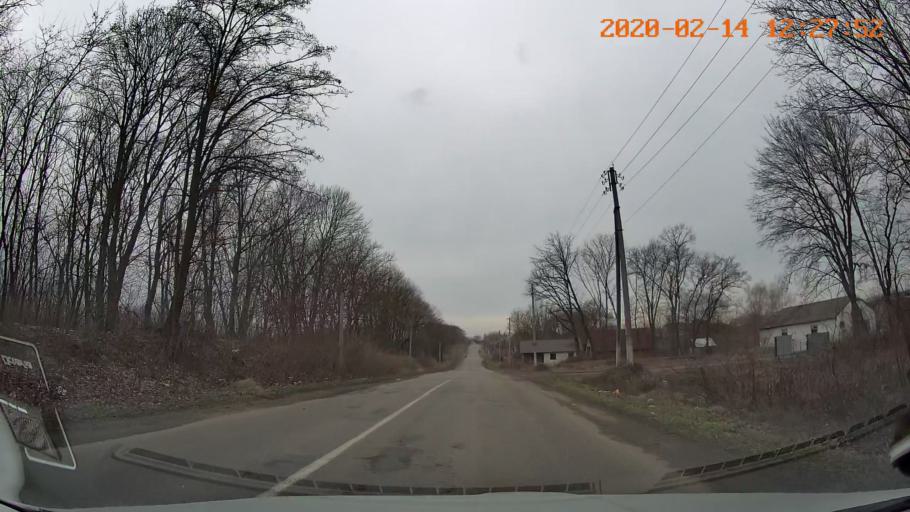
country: RO
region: Botosani
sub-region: Comuna Paltinis
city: Paltinis
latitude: 48.2595
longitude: 26.6041
